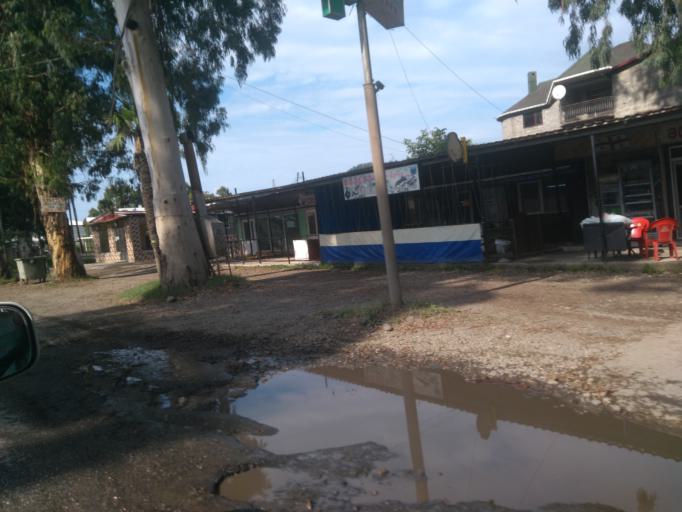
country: GE
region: Ajaria
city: Khelvachauri
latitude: 41.5927
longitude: 41.6443
